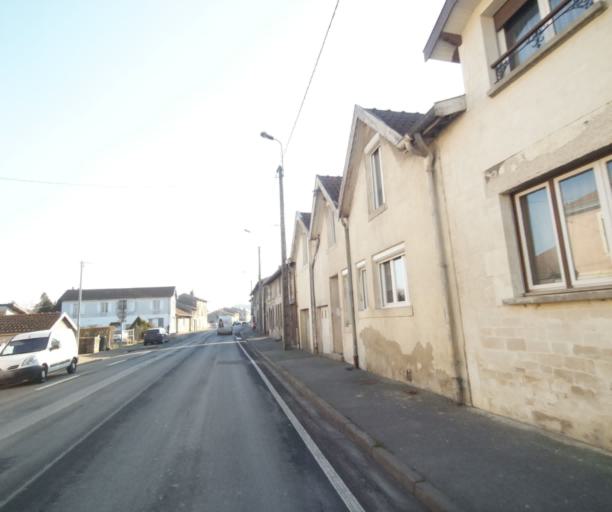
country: FR
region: Champagne-Ardenne
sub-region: Departement de la Haute-Marne
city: Chevillon
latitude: 48.5247
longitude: 5.1029
